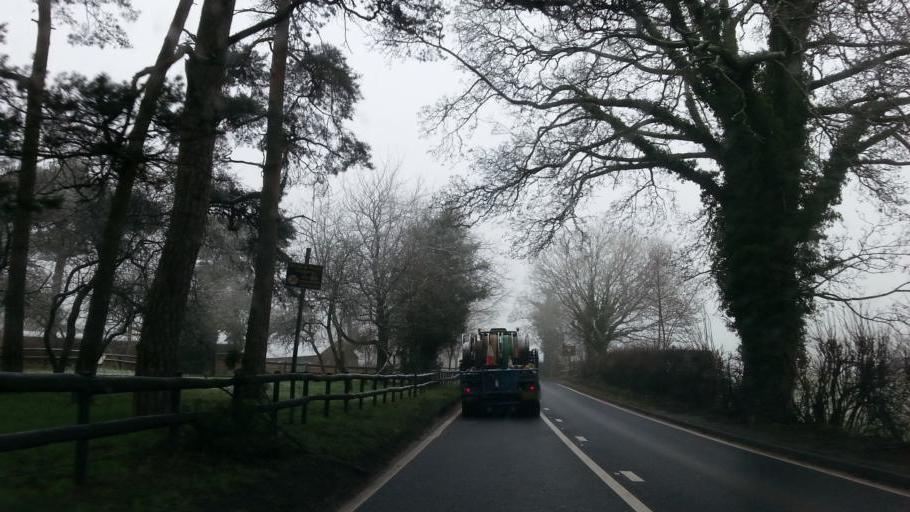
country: GB
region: England
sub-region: Cheshire East
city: Siddington
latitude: 53.2136
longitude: -2.2291
